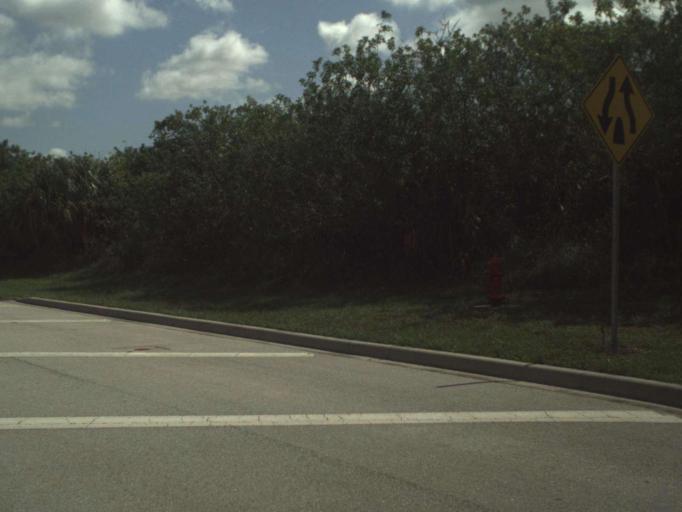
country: US
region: Florida
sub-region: Saint Lucie County
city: Port Saint Lucie
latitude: 27.2108
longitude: -80.3719
